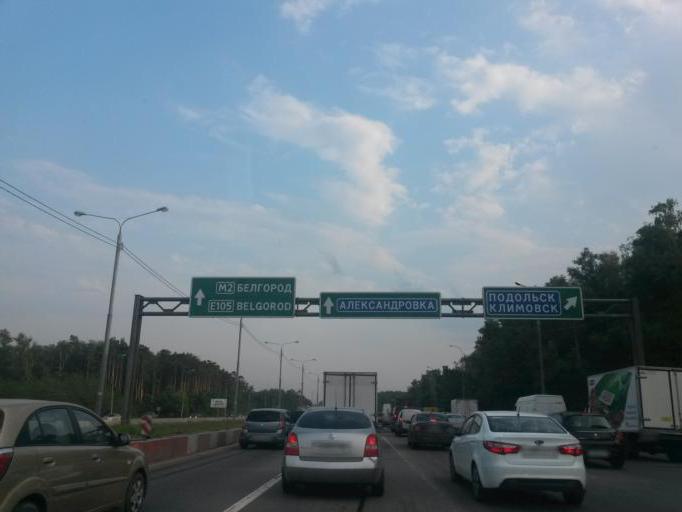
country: RU
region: Moskovskaya
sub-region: Podol'skiy Rayon
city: Podol'sk
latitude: 55.4118
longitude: 37.6073
